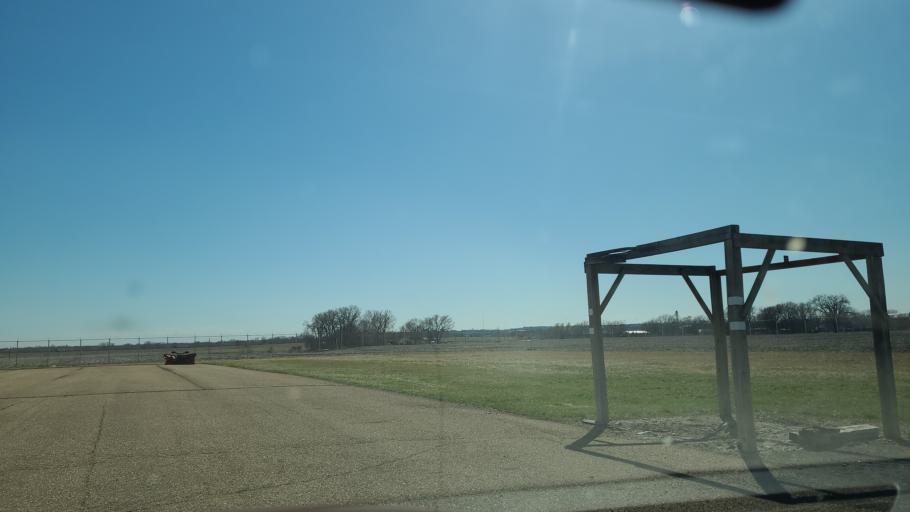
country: US
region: Kansas
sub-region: Douglas County
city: Lawrence
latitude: 39.0041
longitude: -95.2188
